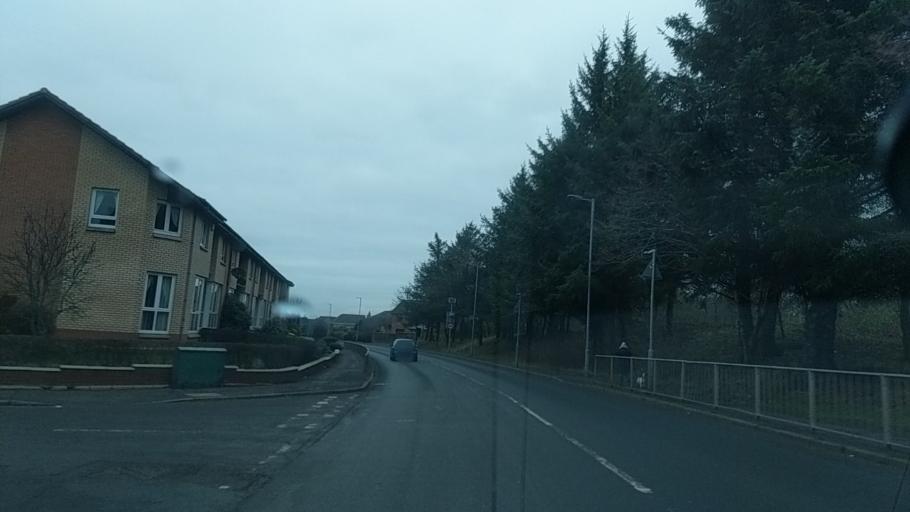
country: GB
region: Scotland
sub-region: South Lanarkshire
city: Rutherglen
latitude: 55.8125
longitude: -4.1850
